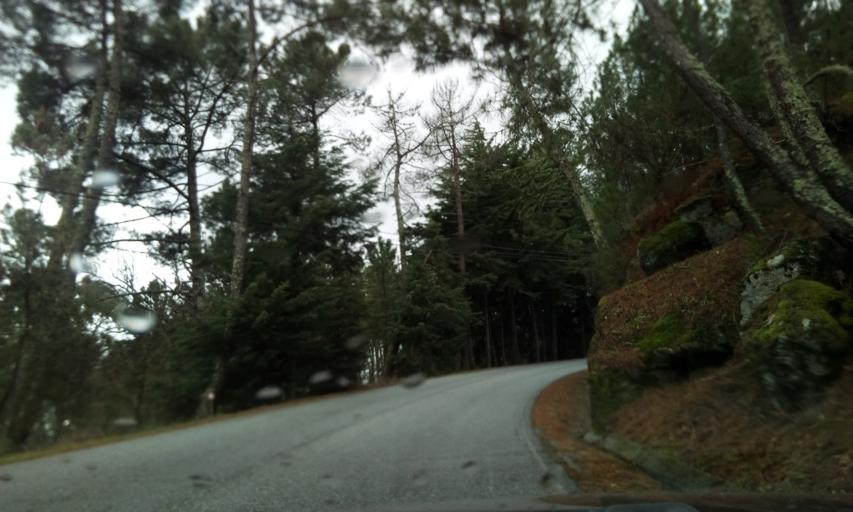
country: PT
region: Guarda
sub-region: Fornos de Algodres
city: Fornos de Algodres
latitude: 40.6245
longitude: -7.5919
